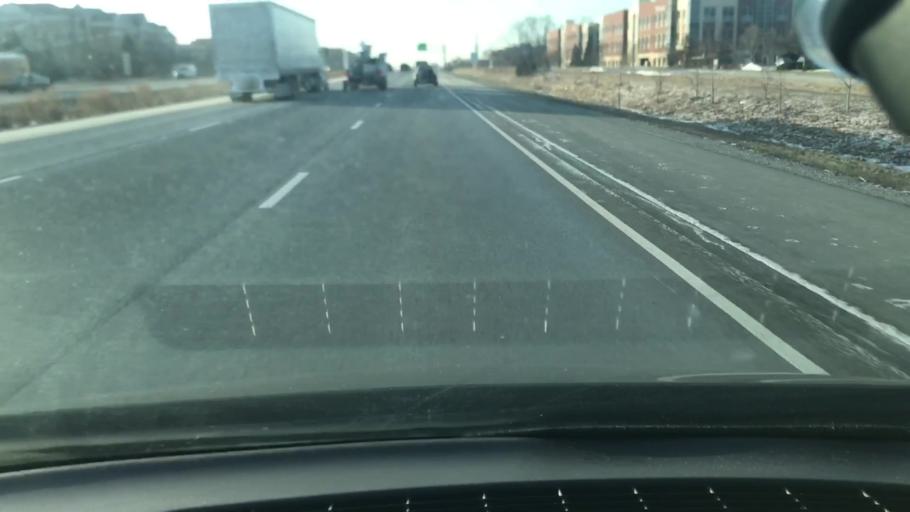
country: US
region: Indiana
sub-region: Hamilton County
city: Carmel
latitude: 39.9699
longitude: -86.1580
